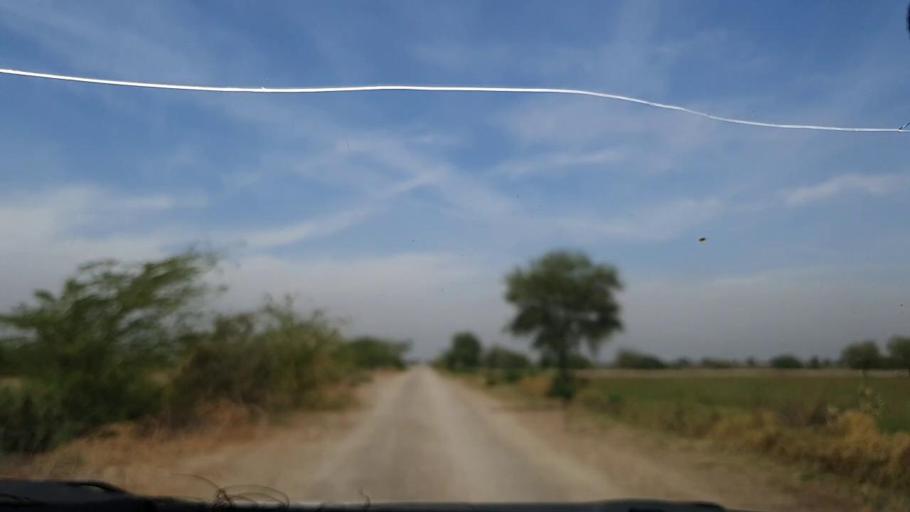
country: PK
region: Sindh
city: Pithoro
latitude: 25.4810
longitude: 69.4555
